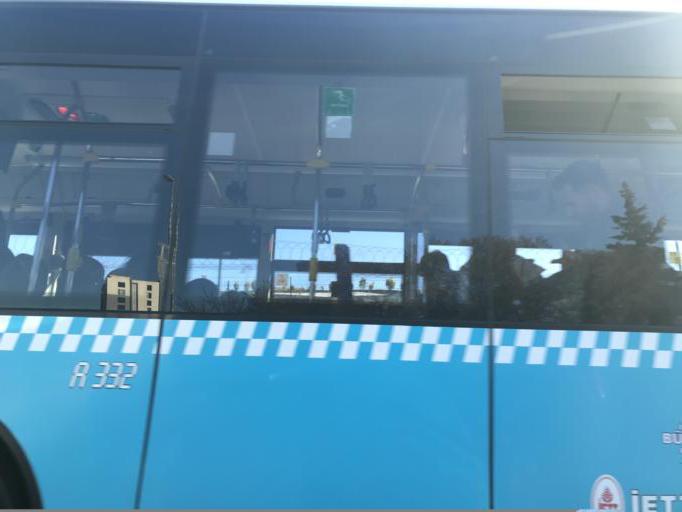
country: TR
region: Istanbul
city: Mahmutbey
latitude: 41.0345
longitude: 28.7835
